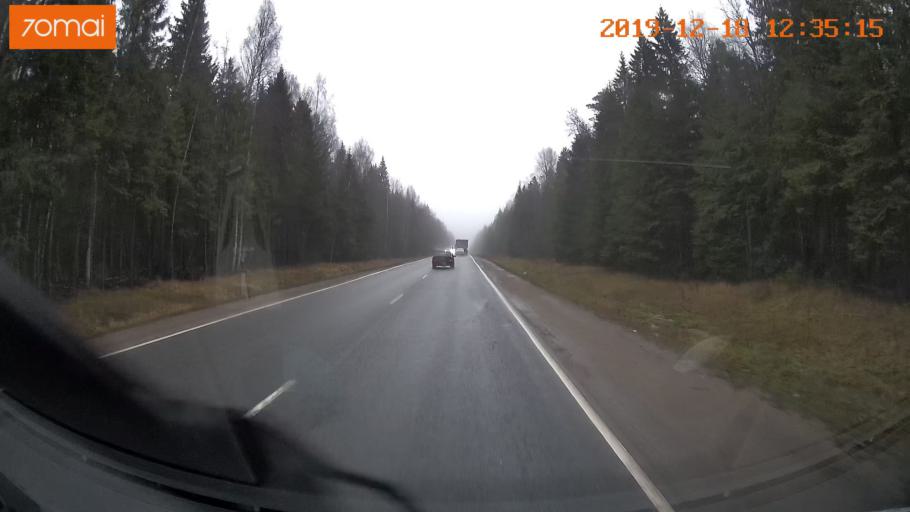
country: RU
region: Moskovskaya
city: Rumyantsevo
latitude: 56.1276
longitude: 36.5808
